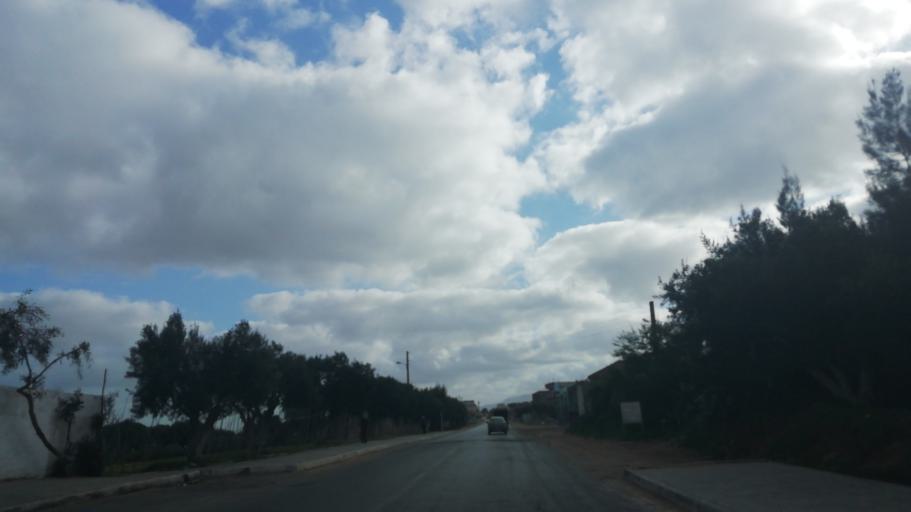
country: DZ
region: Relizane
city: Mazouna
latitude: 36.2603
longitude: 0.6079
